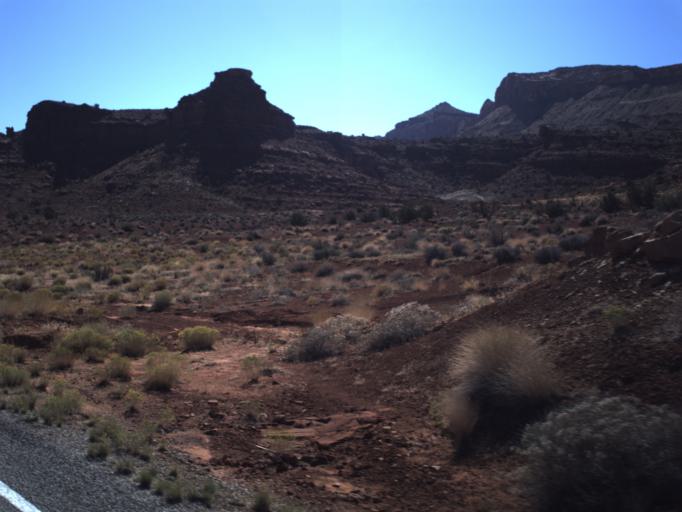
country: US
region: Utah
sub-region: San Juan County
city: Blanding
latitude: 37.8091
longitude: -110.3286
